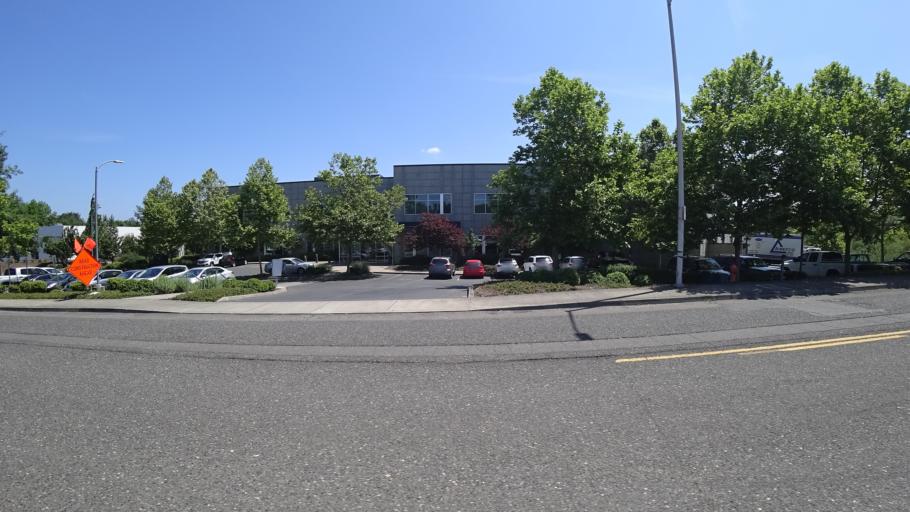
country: US
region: Oregon
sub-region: Multnomah County
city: Fairview
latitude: 45.5533
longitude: -122.4899
